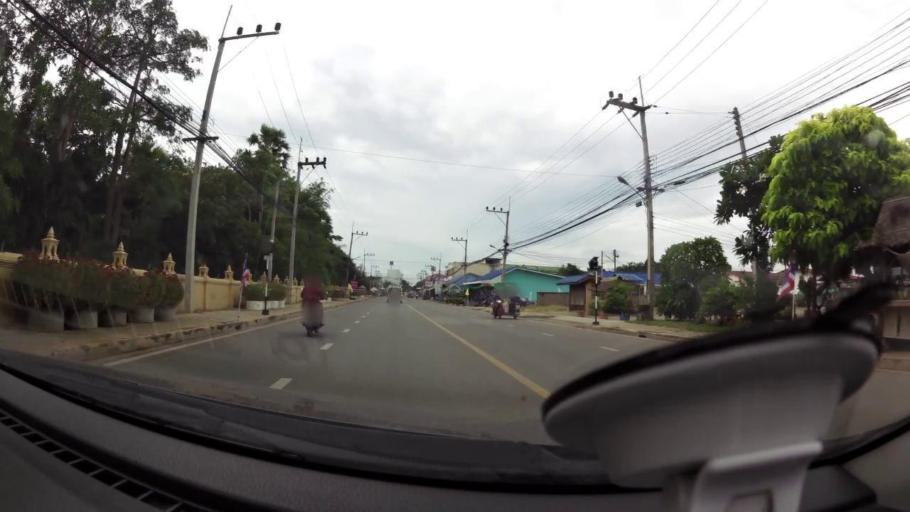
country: TH
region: Prachuap Khiri Khan
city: Pran Buri
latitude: 12.3959
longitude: 99.9897
